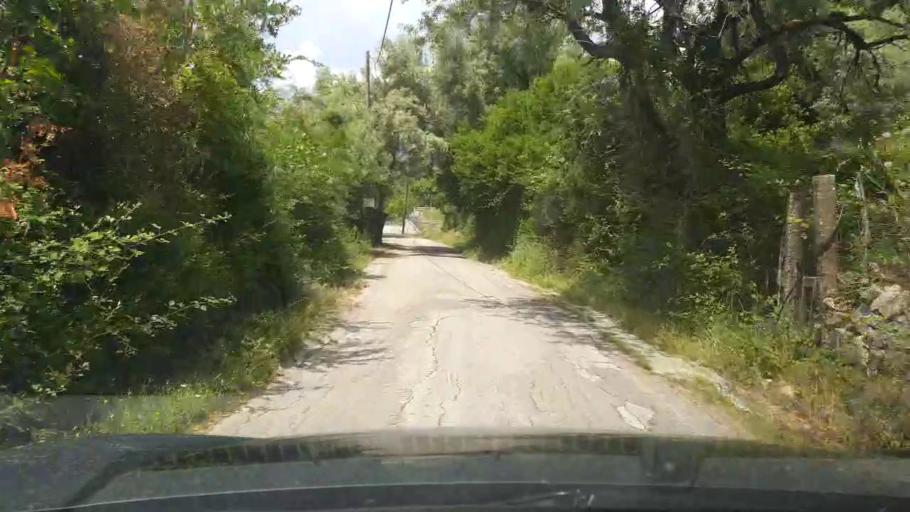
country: GR
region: Ionian Islands
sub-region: Lefkada
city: Nidri
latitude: 38.6436
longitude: 20.7060
